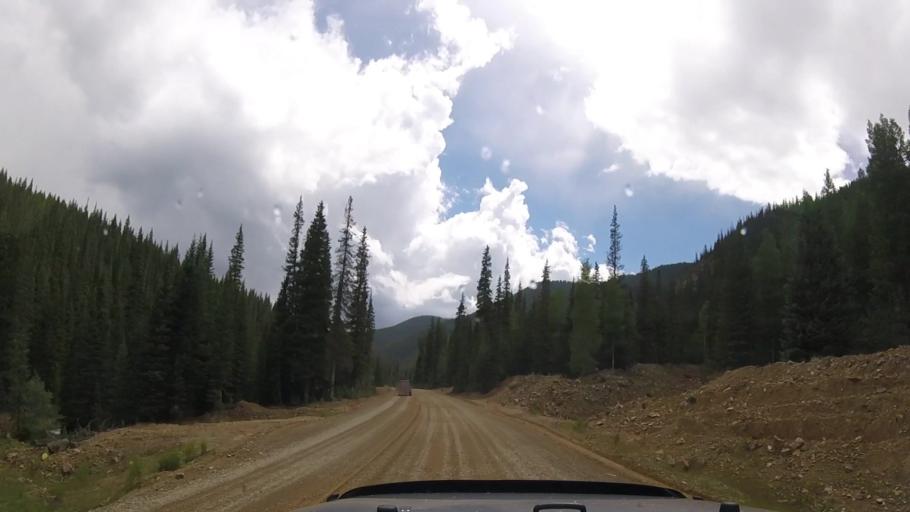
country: US
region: Colorado
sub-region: San Juan County
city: Silverton
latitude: 37.8462
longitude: -107.6787
